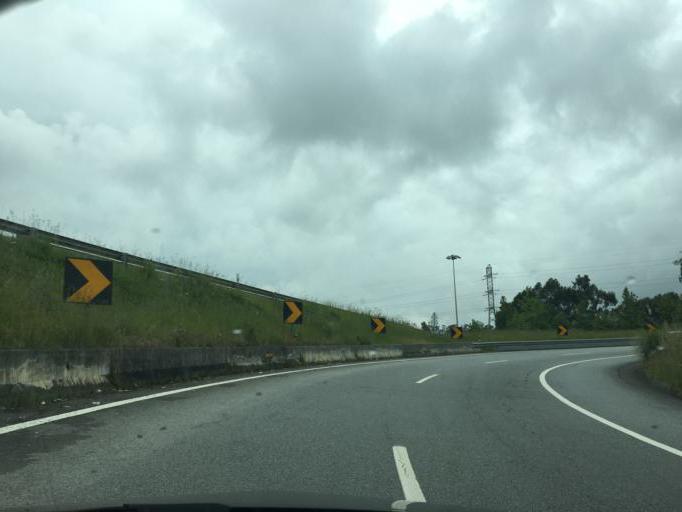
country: PT
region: Porto
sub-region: Porto
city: Porto
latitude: 41.1723
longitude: -8.6232
